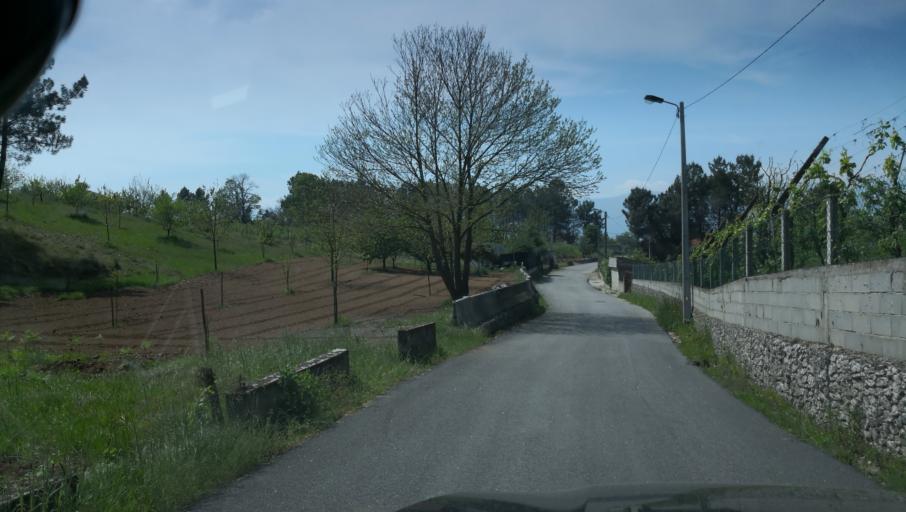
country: PT
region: Vila Real
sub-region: Vila Real
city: Vila Real
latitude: 41.2823
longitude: -7.7066
